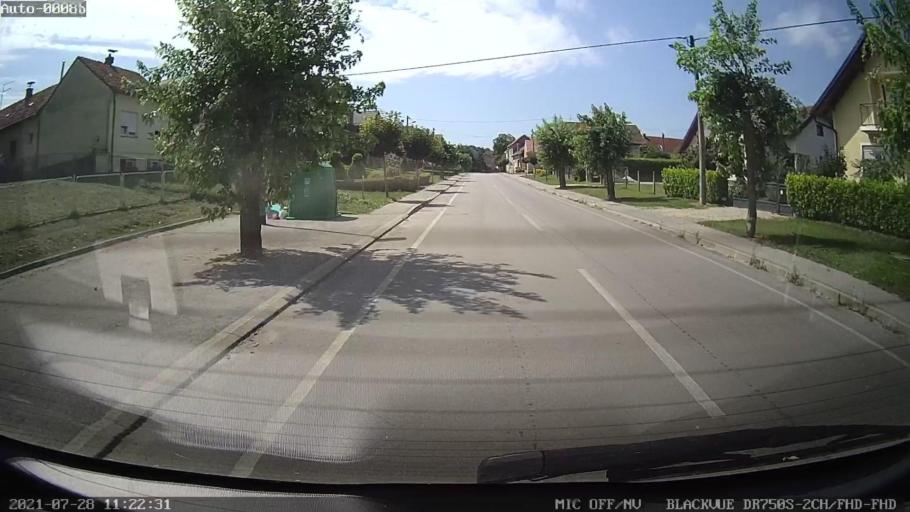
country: HR
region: Varazdinska
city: Jalzabet
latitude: 46.2590
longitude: 16.4742
